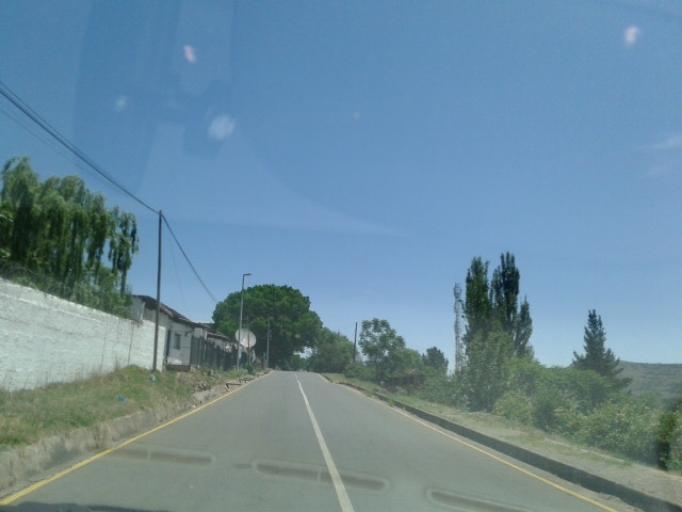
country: LS
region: Maseru
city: Maseru
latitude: -29.3017
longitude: 27.4781
